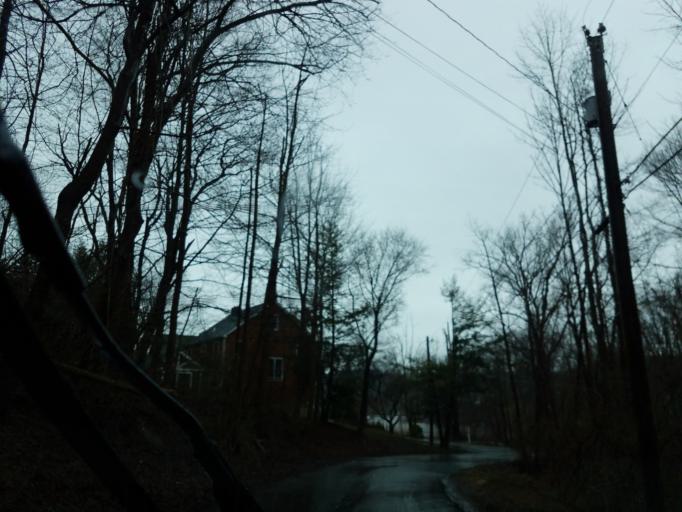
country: US
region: Connecticut
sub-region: Fairfield County
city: Ridgefield
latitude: 41.3378
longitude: -73.4914
